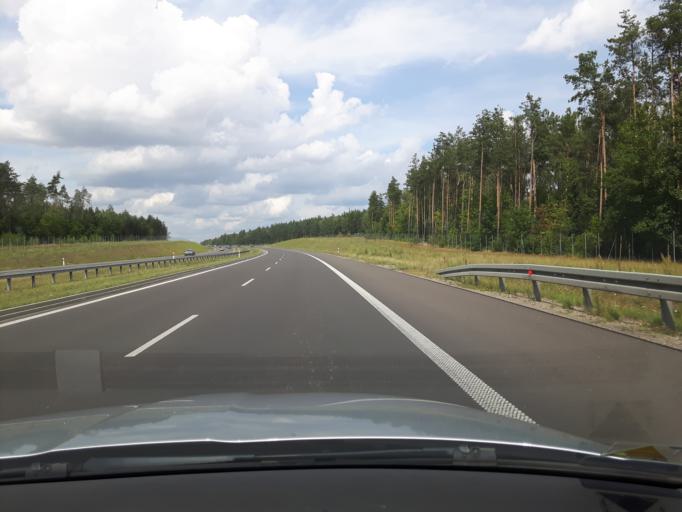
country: PL
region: Masovian Voivodeship
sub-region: Powiat mlawski
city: Wieczfnia Koscielna
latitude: 53.2384
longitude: 20.4232
